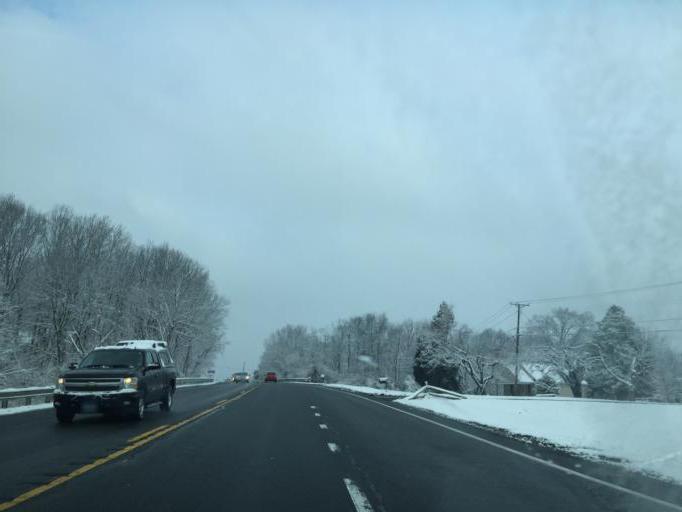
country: US
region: Maryland
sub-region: Harford County
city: Joppatowne
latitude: 39.4628
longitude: -76.3653
